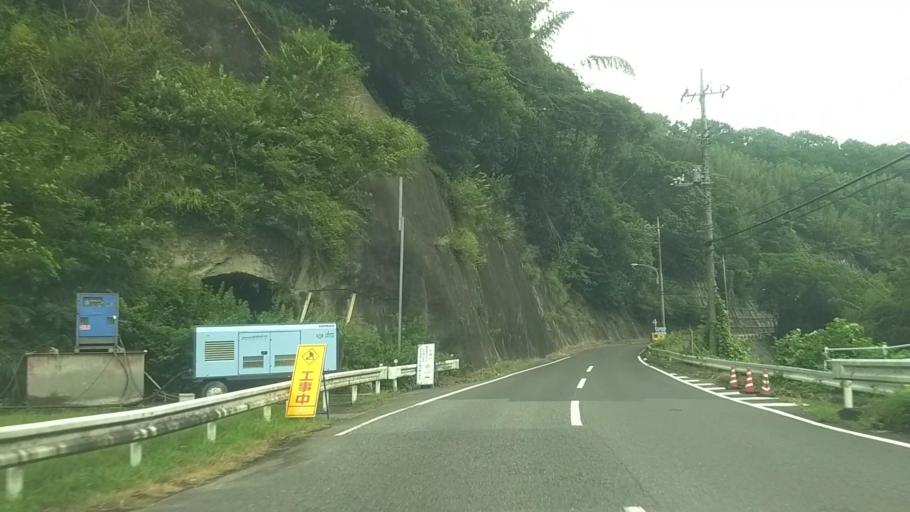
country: JP
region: Chiba
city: Kimitsu
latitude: 35.2488
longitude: 139.9917
